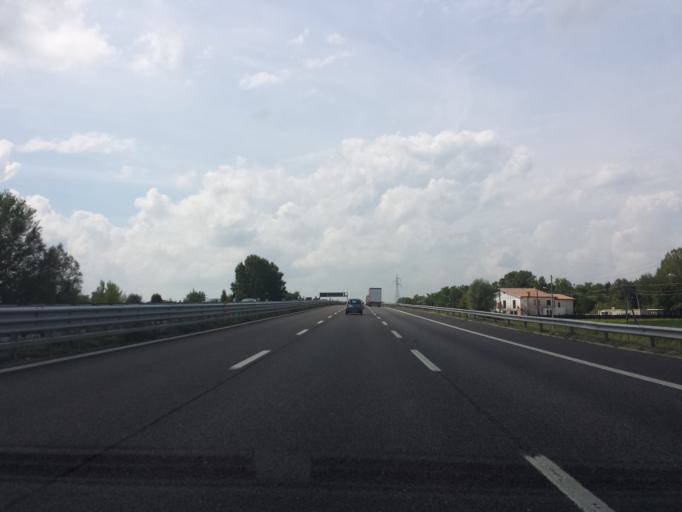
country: IT
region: Veneto
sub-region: Provincia di Padova
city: Villaguattera
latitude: 45.4501
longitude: 11.8364
